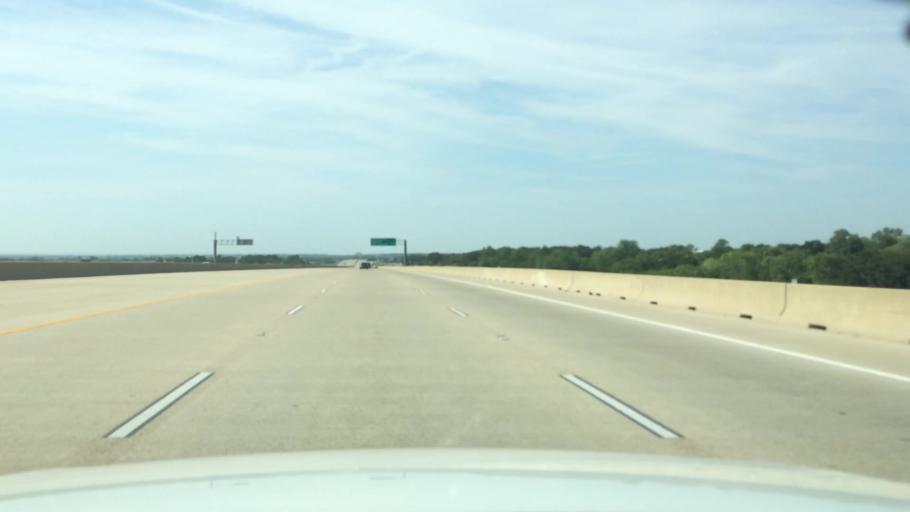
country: US
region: Texas
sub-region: Tarrant County
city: Euless
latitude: 32.8157
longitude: -97.0187
